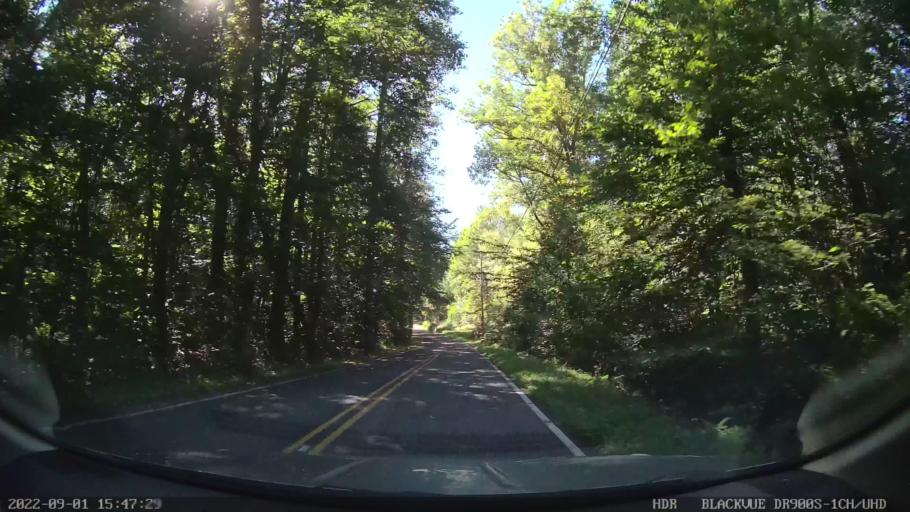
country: US
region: Pennsylvania
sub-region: Berks County
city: Topton
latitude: 40.4712
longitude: -75.7200
